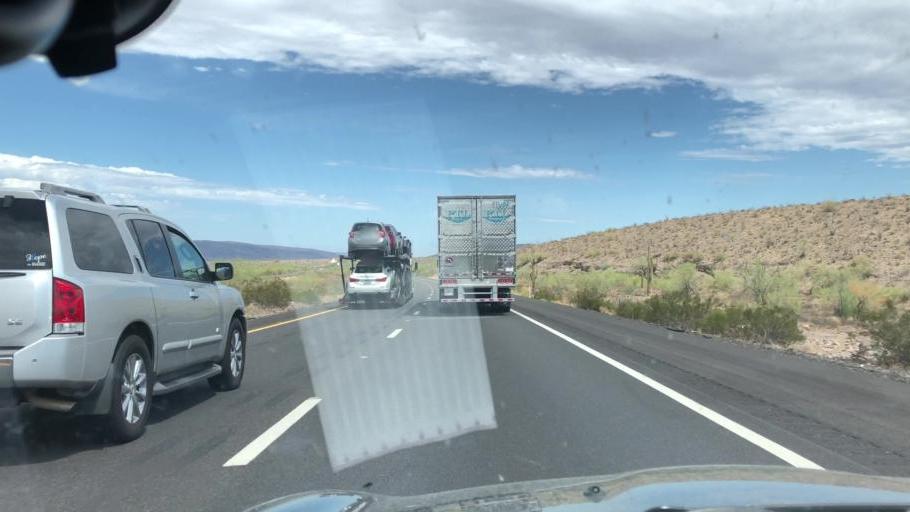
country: US
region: Arizona
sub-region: La Paz County
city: Quartzsite
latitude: 33.6636
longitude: -114.0281
